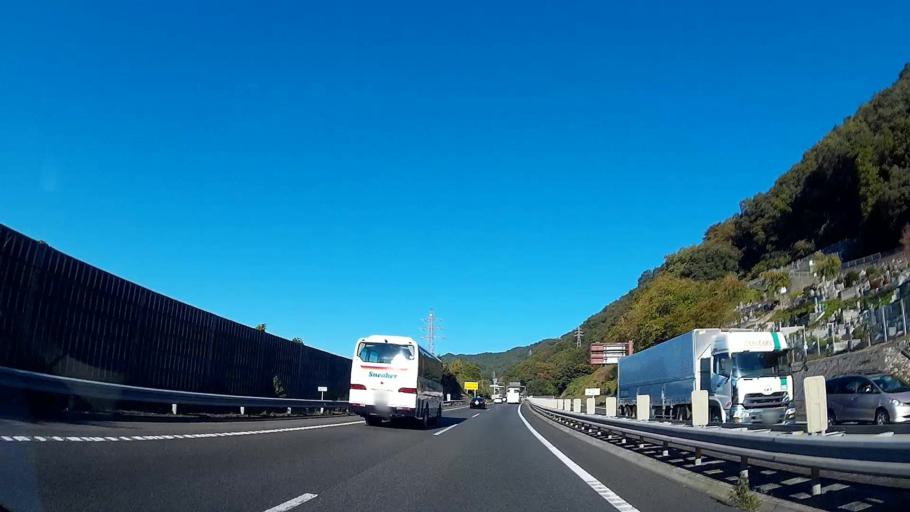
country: JP
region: Yamanashi
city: Uenohara
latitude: 35.6191
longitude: 139.1833
